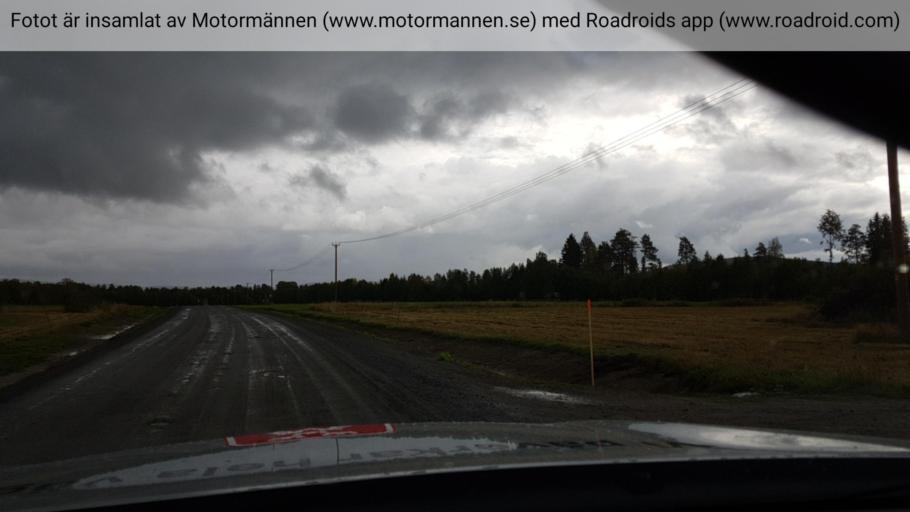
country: SE
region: Norrbotten
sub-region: Alvsbyns Kommun
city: AElvsbyn
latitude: 65.9093
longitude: 21.2882
